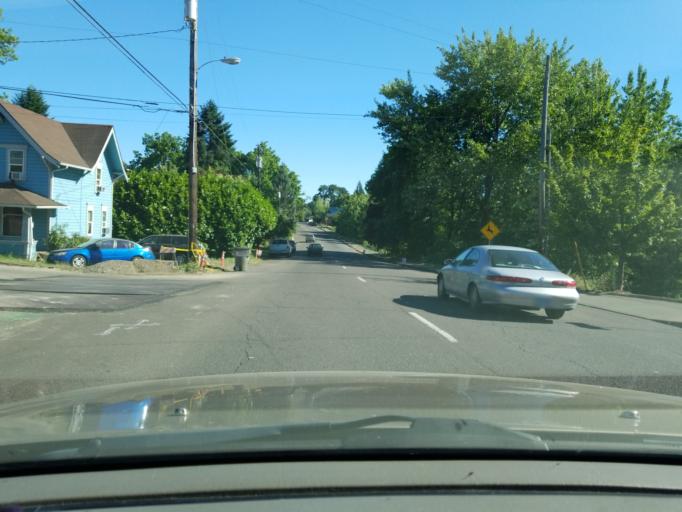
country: US
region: Oregon
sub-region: Yamhill County
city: McMinnville
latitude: 45.2087
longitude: -123.1991
